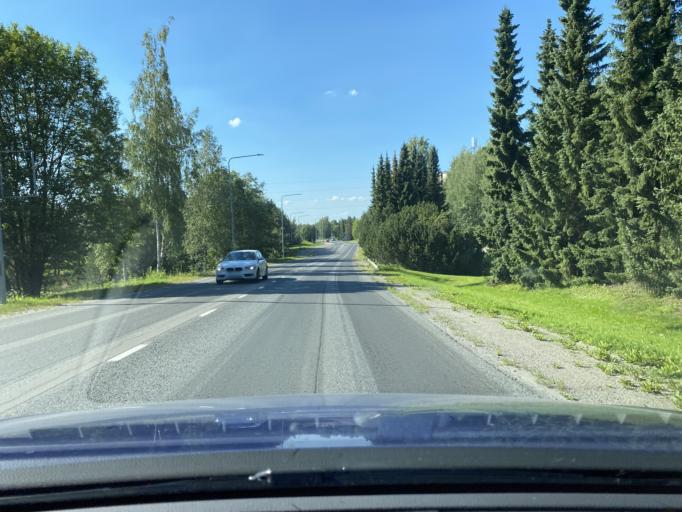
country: FI
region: Pirkanmaa
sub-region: Tampere
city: Tampere
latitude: 61.4902
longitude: 23.8519
